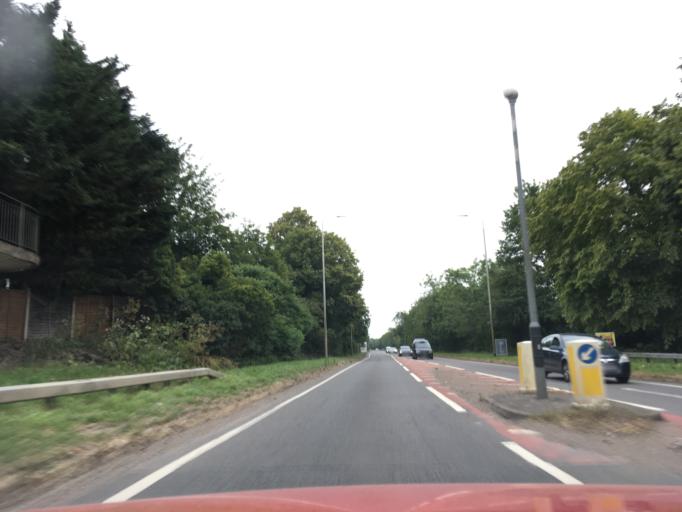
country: GB
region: England
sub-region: Hertfordshire
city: Markyate
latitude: 51.8362
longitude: -0.4572
